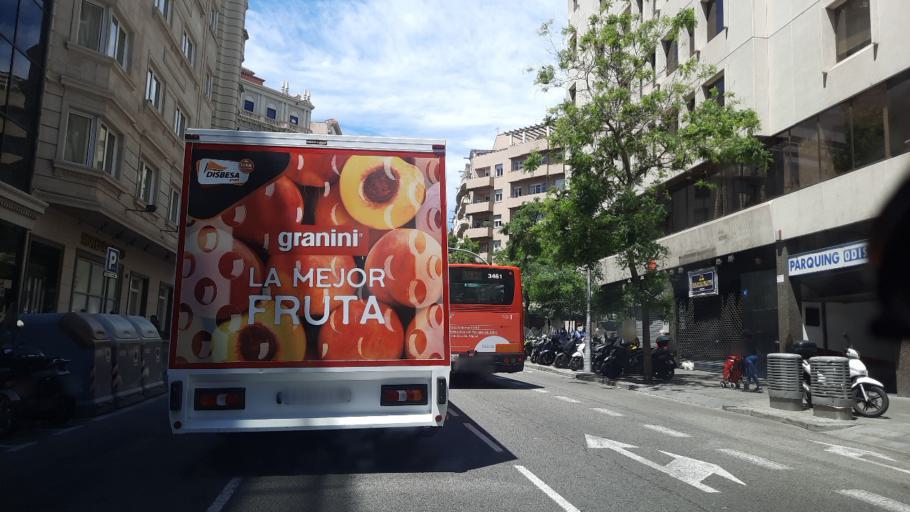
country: ES
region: Catalonia
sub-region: Provincia de Barcelona
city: Gracia
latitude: 41.3955
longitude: 2.1498
